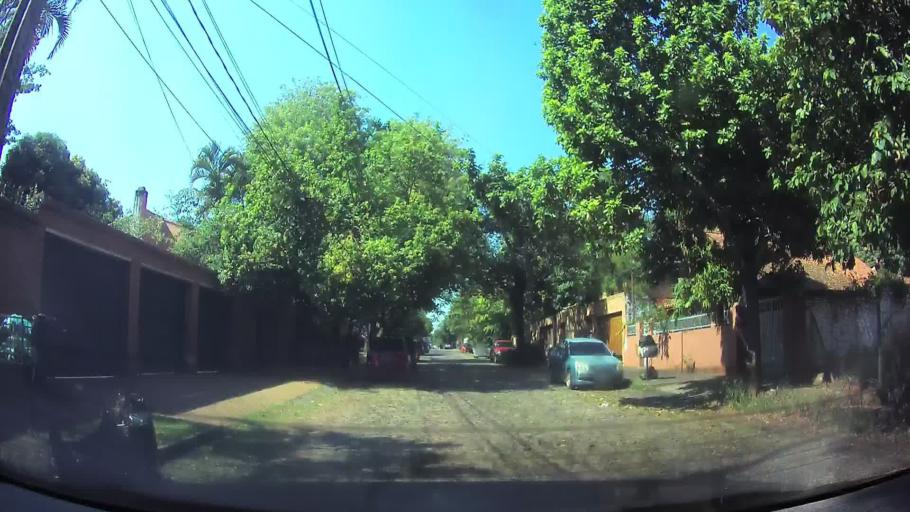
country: PY
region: Central
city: Fernando de la Mora
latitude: -25.2881
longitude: -57.5606
